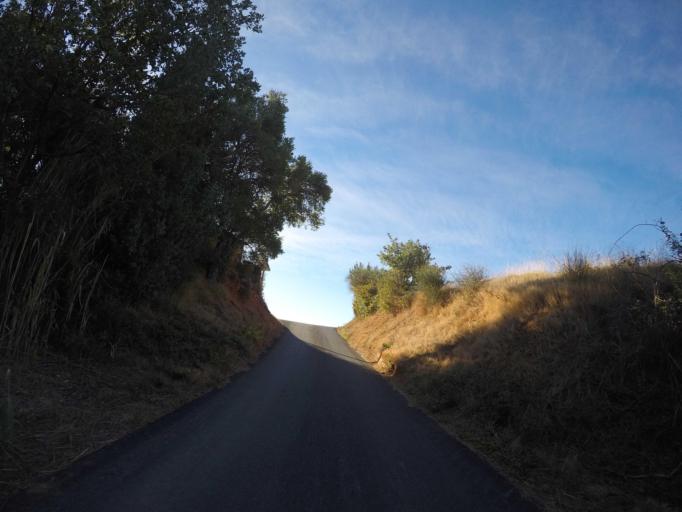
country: FR
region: Languedoc-Roussillon
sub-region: Departement des Pyrenees-Orientales
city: Llupia
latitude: 42.5938
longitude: 2.7640
